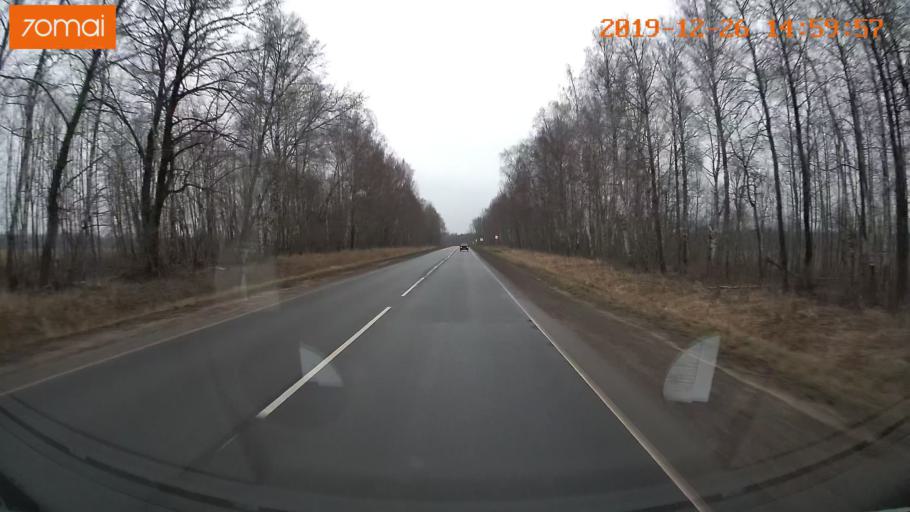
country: RU
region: Jaroslavl
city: Rybinsk
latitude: 58.2520
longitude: 38.8491
